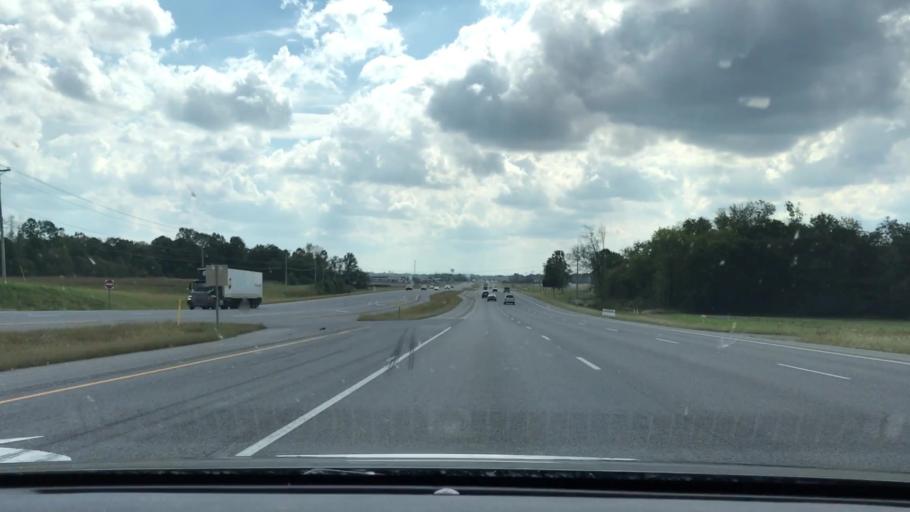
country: US
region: Kentucky
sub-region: Christian County
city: Oak Grove
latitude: 36.6821
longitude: -87.4484
